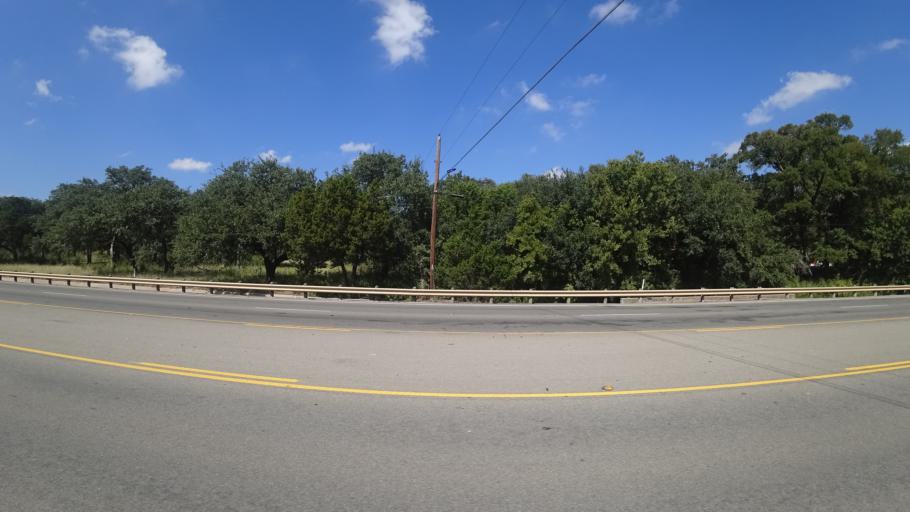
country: US
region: Texas
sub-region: Williamson County
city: Brushy Creek
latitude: 30.4833
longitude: -97.7398
